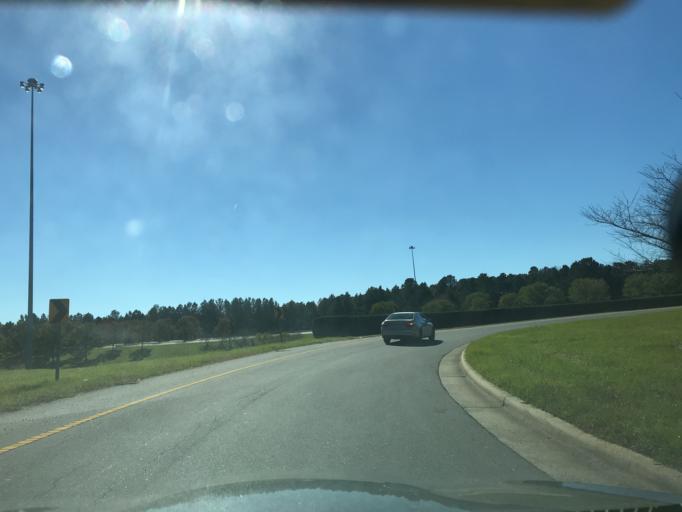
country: US
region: North Carolina
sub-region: Wake County
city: Morrisville
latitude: 35.8642
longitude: -78.8028
